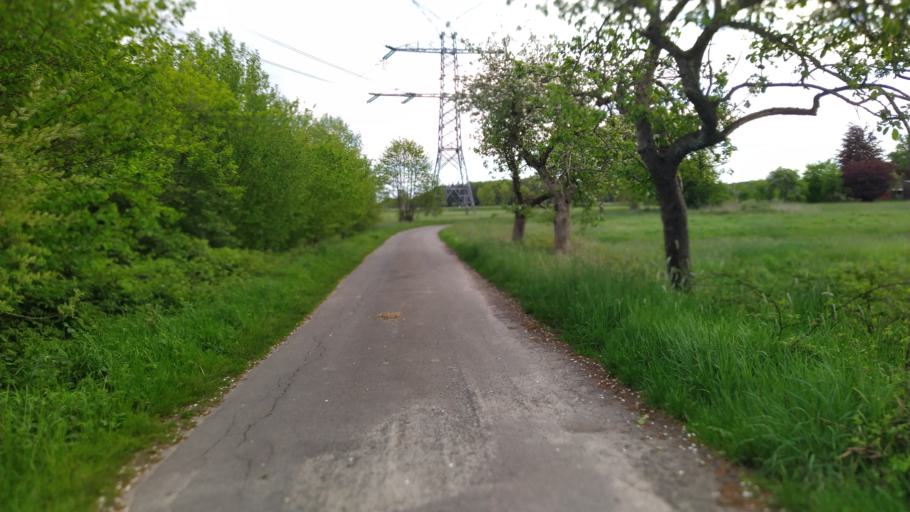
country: DE
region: Lower Saxony
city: Brest
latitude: 53.4245
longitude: 9.3905
